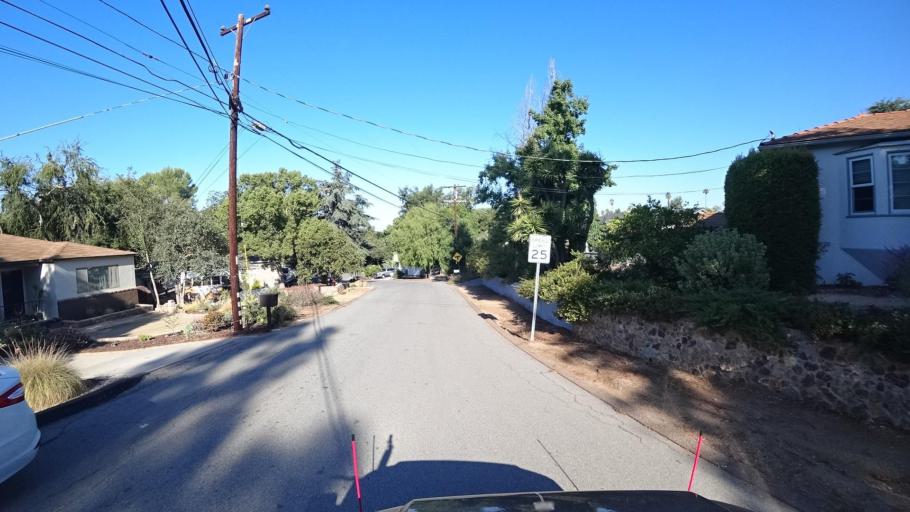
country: US
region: California
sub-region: San Diego County
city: Spring Valley
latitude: 32.7649
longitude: -116.9960
